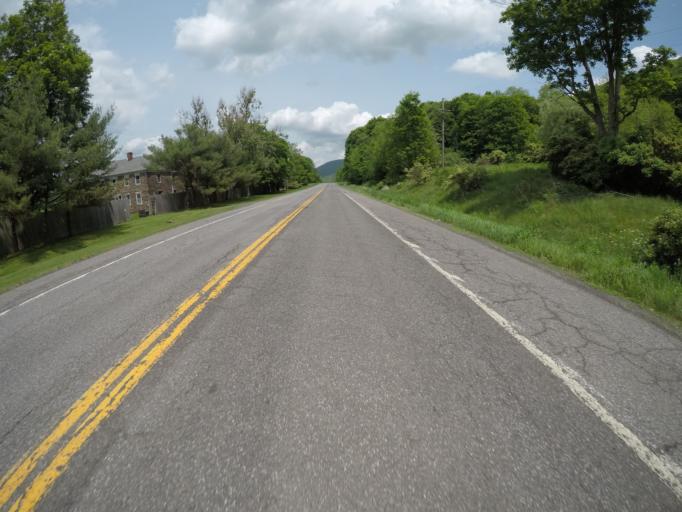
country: US
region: New York
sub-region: Delaware County
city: Stamford
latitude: 42.2617
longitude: -74.5892
